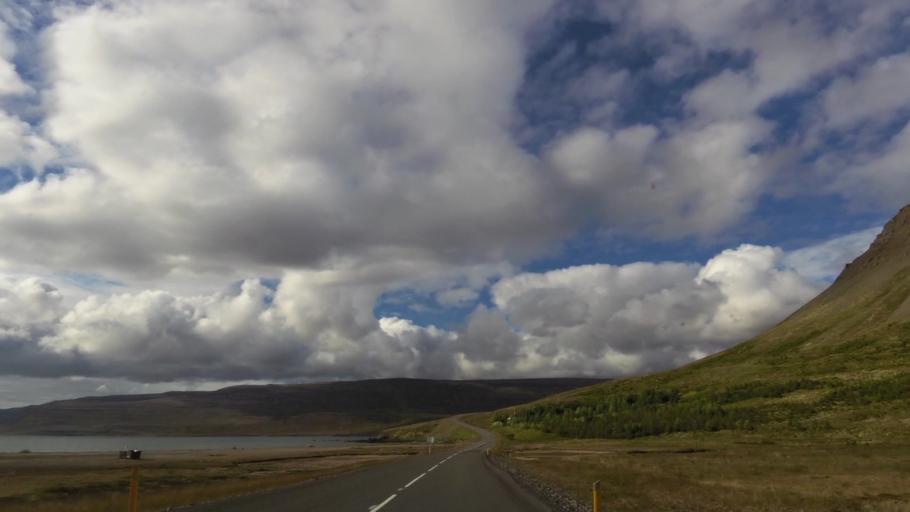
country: IS
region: West
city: Olafsvik
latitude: 65.5162
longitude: -23.8346
